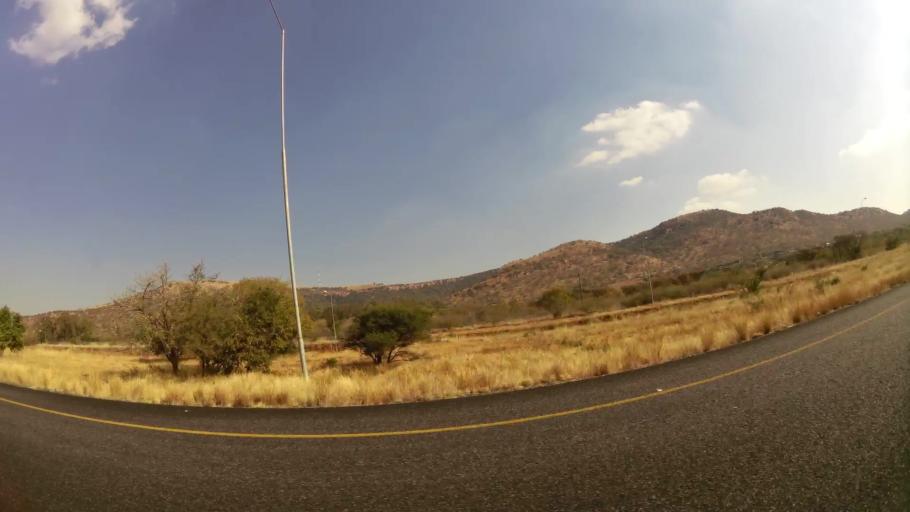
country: ZA
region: North-West
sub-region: Bojanala Platinum District Municipality
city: Rustenburg
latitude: -25.5991
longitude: 27.1316
